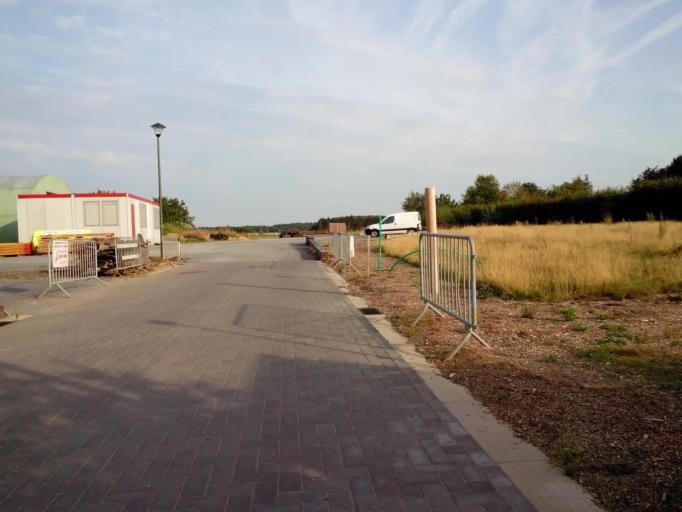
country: BE
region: Flanders
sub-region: Provincie Vlaams-Brabant
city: Oud-Heverlee
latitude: 50.8251
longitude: 4.7046
